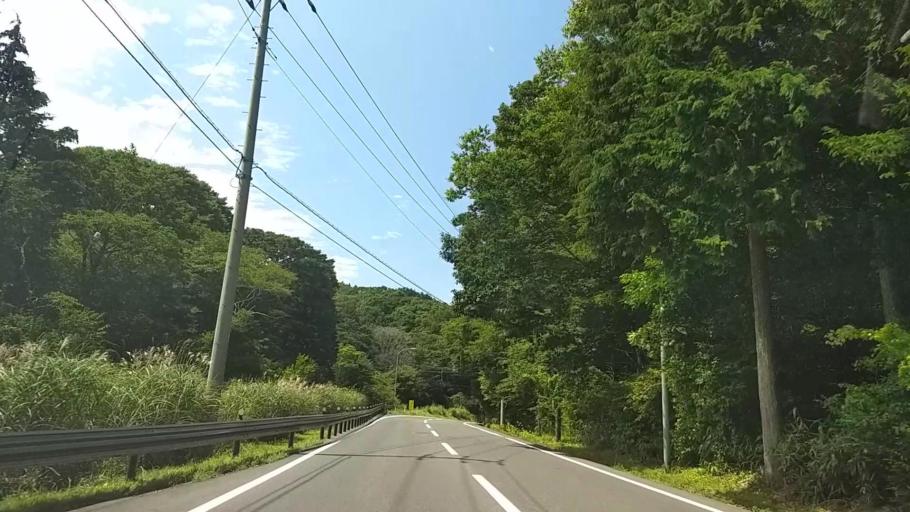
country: JP
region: Shizuoka
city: Fuji
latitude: 35.2560
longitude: 138.7934
